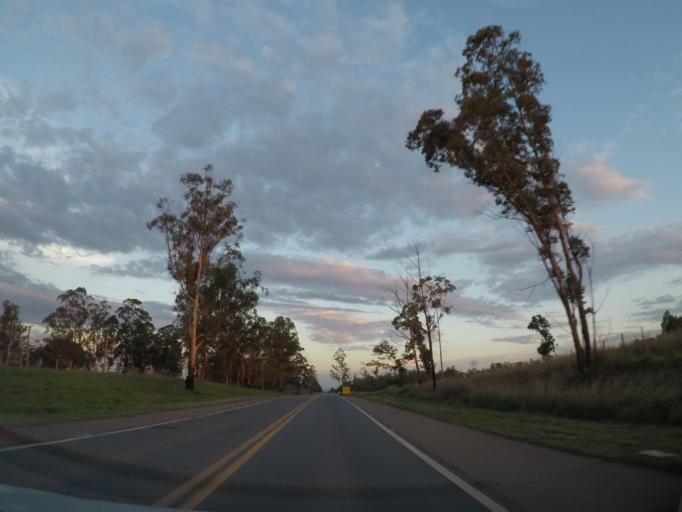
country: BR
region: Sao Paulo
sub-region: Itupeva
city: Itupeva
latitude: -23.0497
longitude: -47.0823
